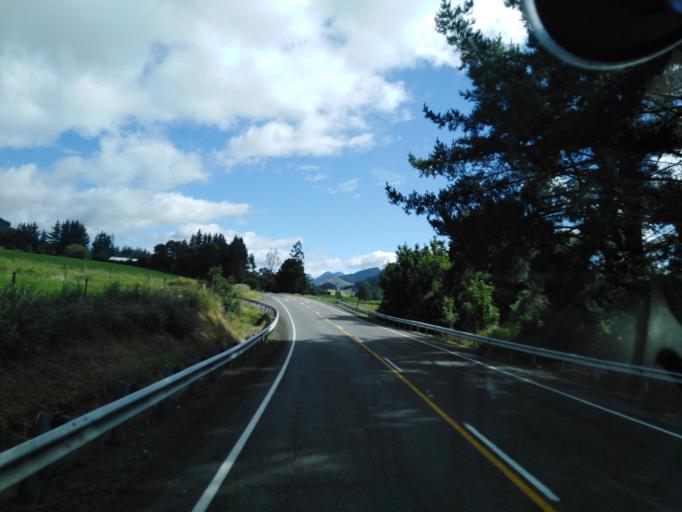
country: NZ
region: Nelson
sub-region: Nelson City
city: Nelson
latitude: -41.2831
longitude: 173.5728
